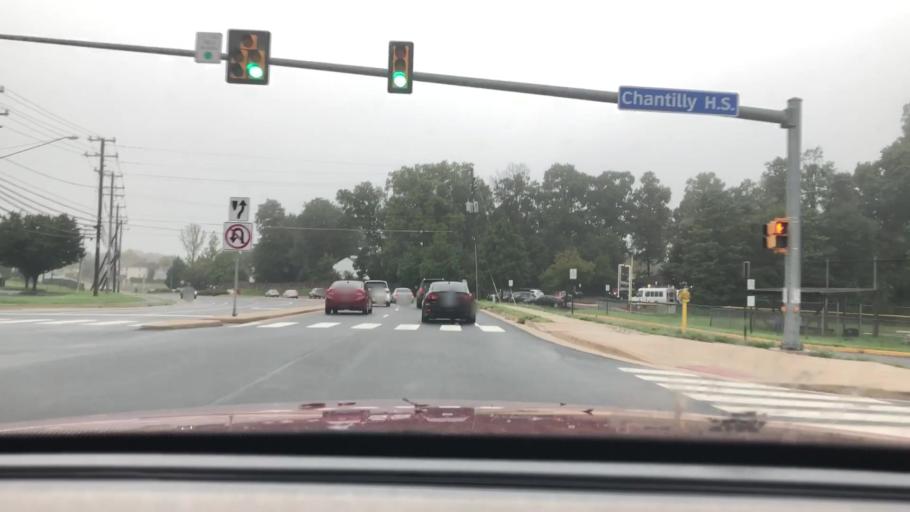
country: US
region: Virginia
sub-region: Fairfax County
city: Greenbriar
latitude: 38.8800
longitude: -77.4086
